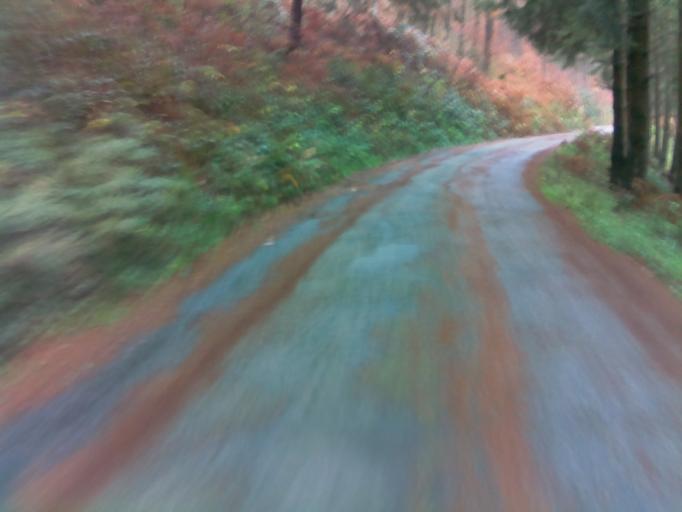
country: DE
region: Baden-Wuerttemberg
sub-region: Karlsruhe Region
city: Heddesbach
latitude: 49.4880
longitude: 8.8485
